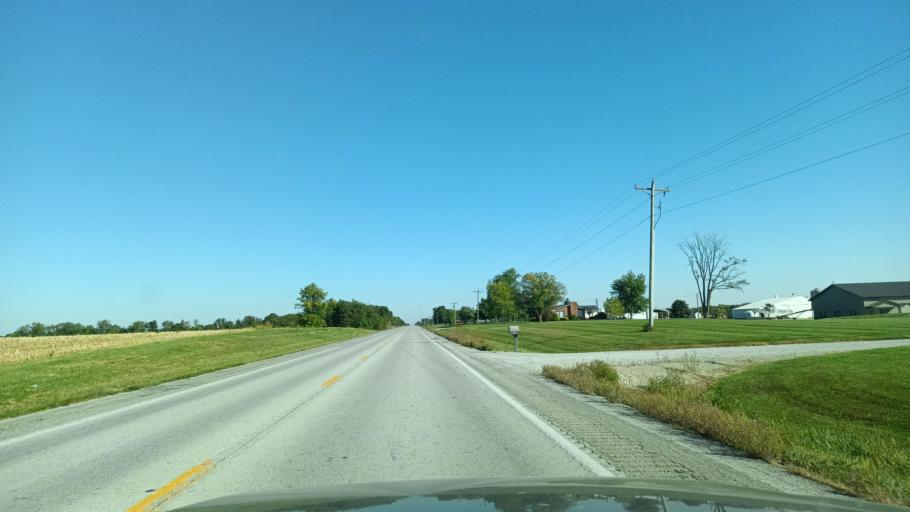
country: US
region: Missouri
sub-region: Audrain County
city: Vandalia
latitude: 39.3774
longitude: -91.6420
